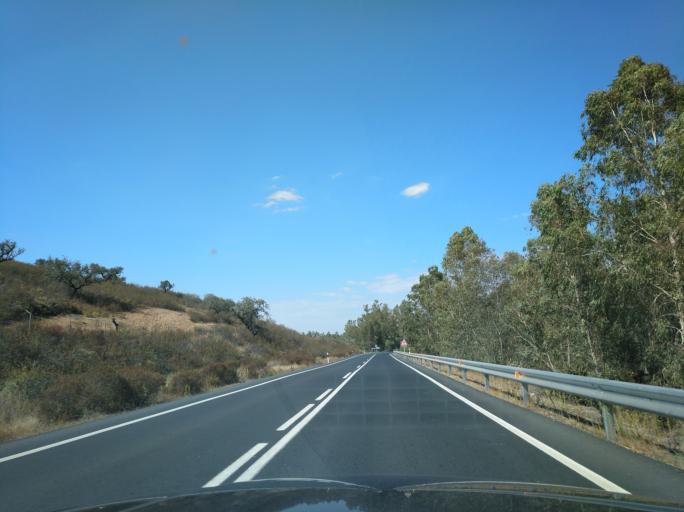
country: ES
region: Andalusia
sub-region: Provincia de Huelva
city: Alosno
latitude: 37.5261
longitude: -7.1346
